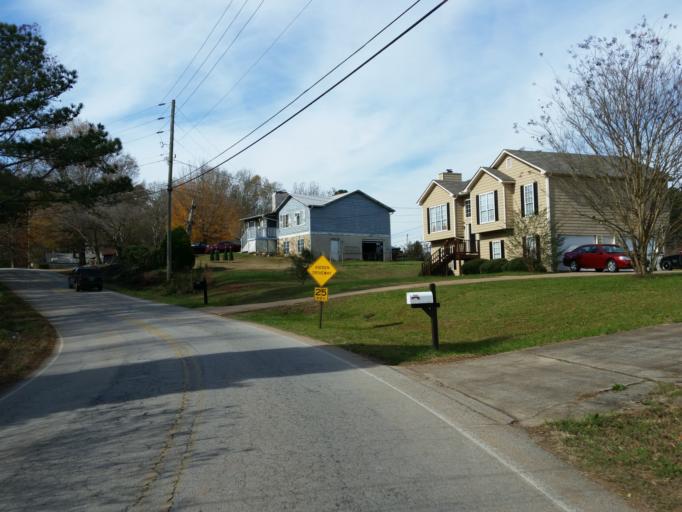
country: US
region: Georgia
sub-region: Douglas County
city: Lithia Springs
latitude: 33.7401
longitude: -84.6726
